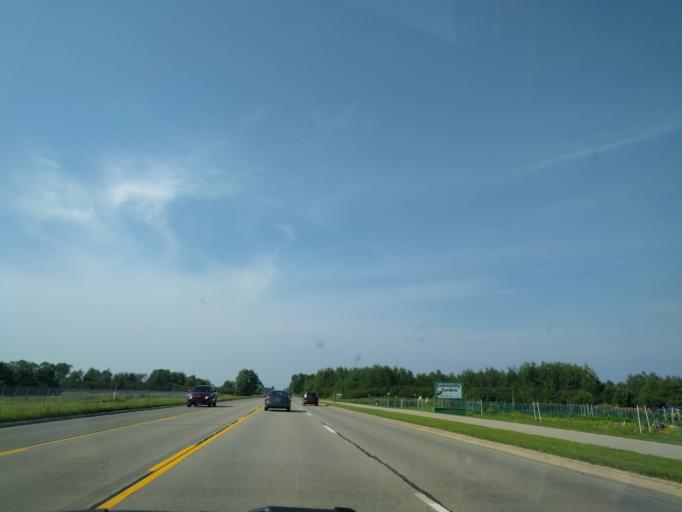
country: US
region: Michigan
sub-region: Delta County
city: Escanaba
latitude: 45.7200
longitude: -87.0801
